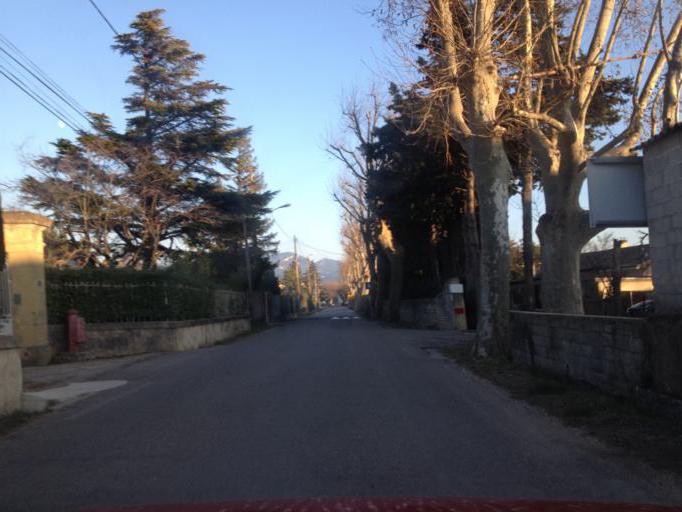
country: FR
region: Provence-Alpes-Cote d'Azur
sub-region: Departement du Vaucluse
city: Violes
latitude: 44.1629
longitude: 4.9484
